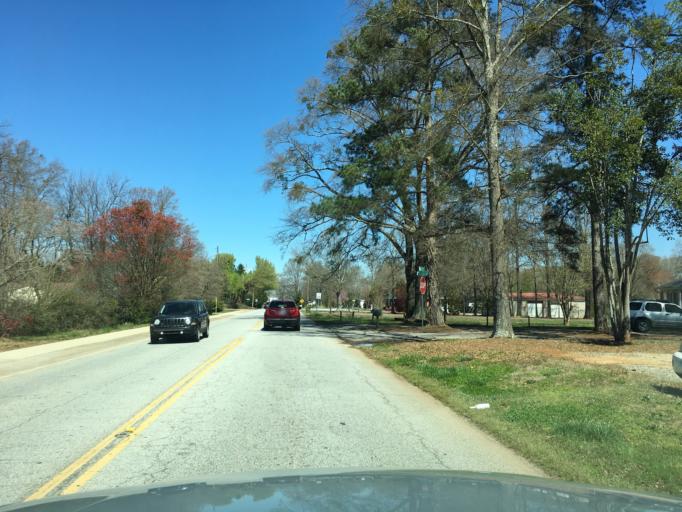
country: US
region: South Carolina
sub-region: Spartanburg County
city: Fairforest
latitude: 34.9279
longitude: -82.0012
